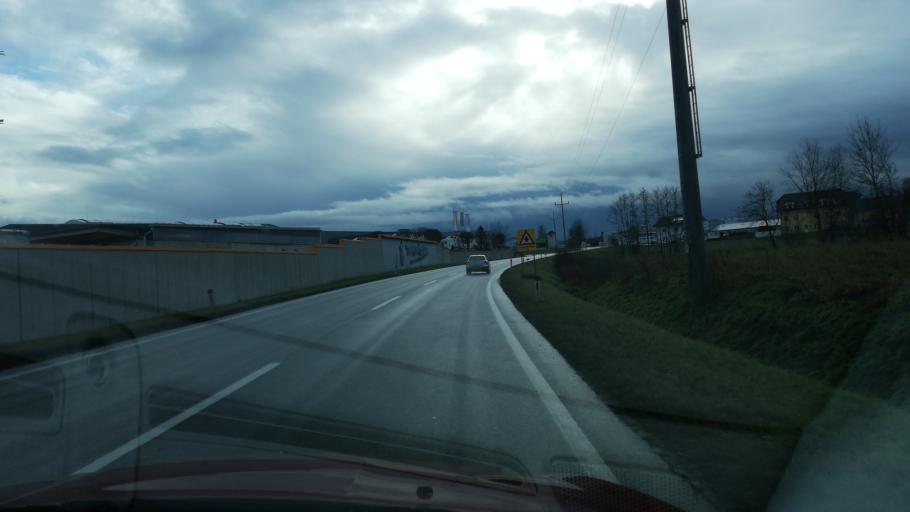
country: AT
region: Upper Austria
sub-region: Wels-Land
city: Sattledt
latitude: 48.0553
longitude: 14.0552
